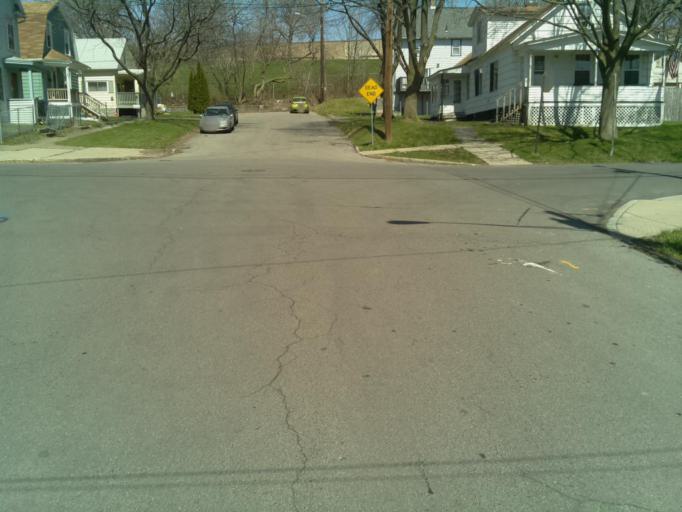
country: US
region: New York
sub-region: Onondaga County
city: Lyncourt
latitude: 43.0561
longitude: -76.1195
